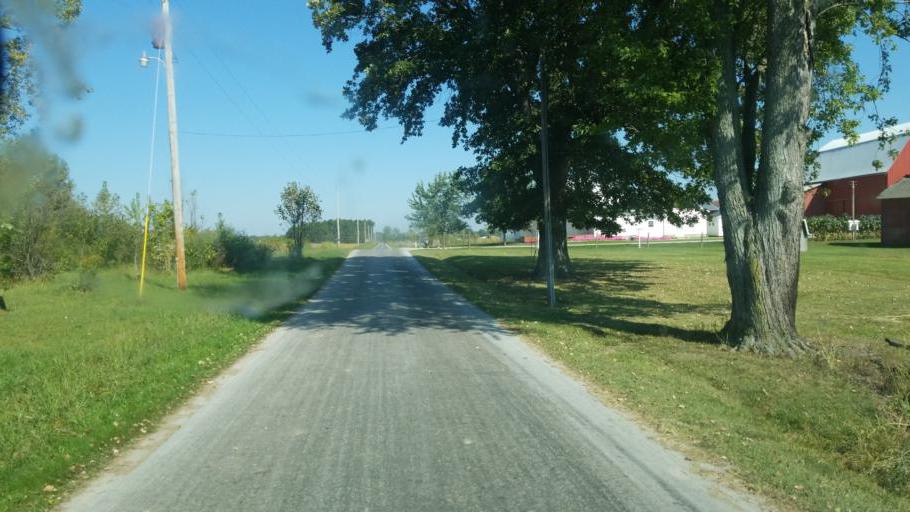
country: US
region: Ohio
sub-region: Hardin County
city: Kenton
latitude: 40.5671
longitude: -83.4874
